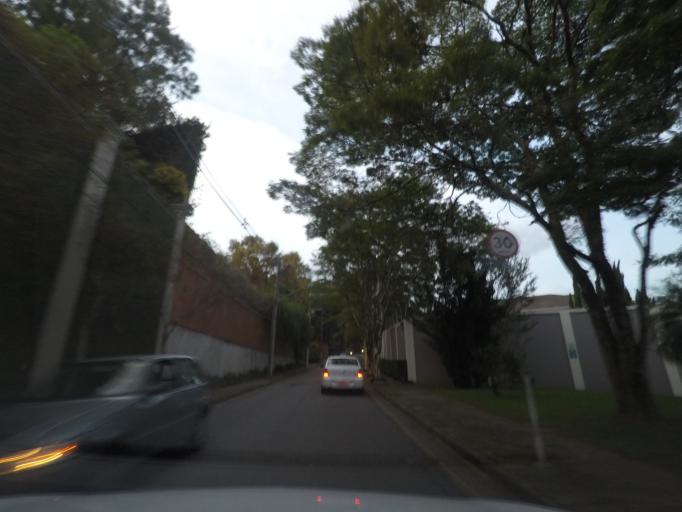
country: BR
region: Sao Paulo
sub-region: Taboao Da Serra
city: Taboao da Serra
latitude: -23.6147
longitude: -46.7116
